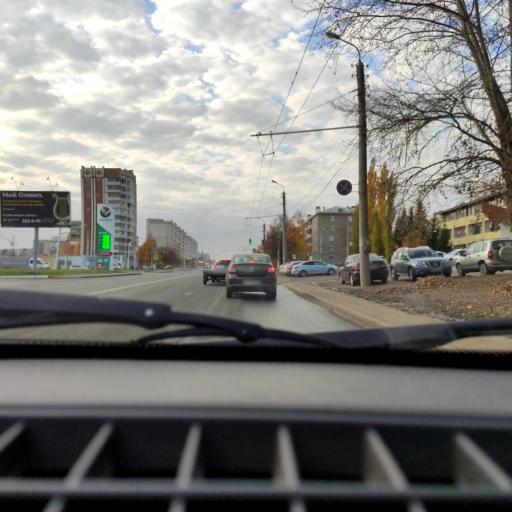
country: RU
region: Bashkortostan
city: Ufa
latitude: 54.7823
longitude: 56.0378
